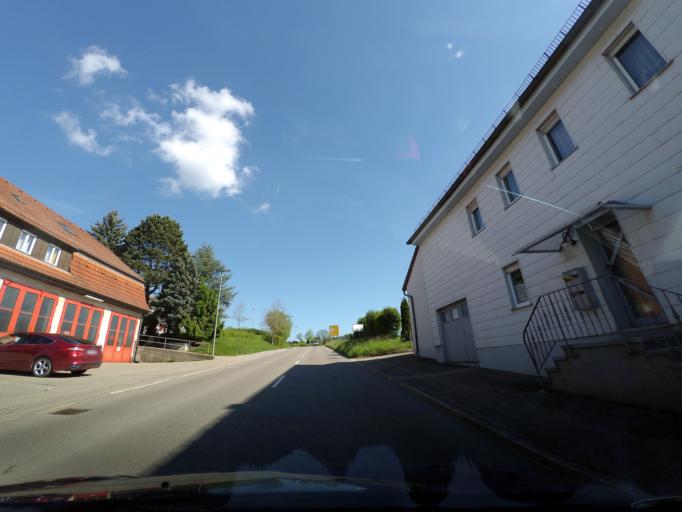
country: DE
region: Baden-Wuerttemberg
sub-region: Regierungsbezirk Stuttgart
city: Gschwend
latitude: 48.9359
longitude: 9.7431
